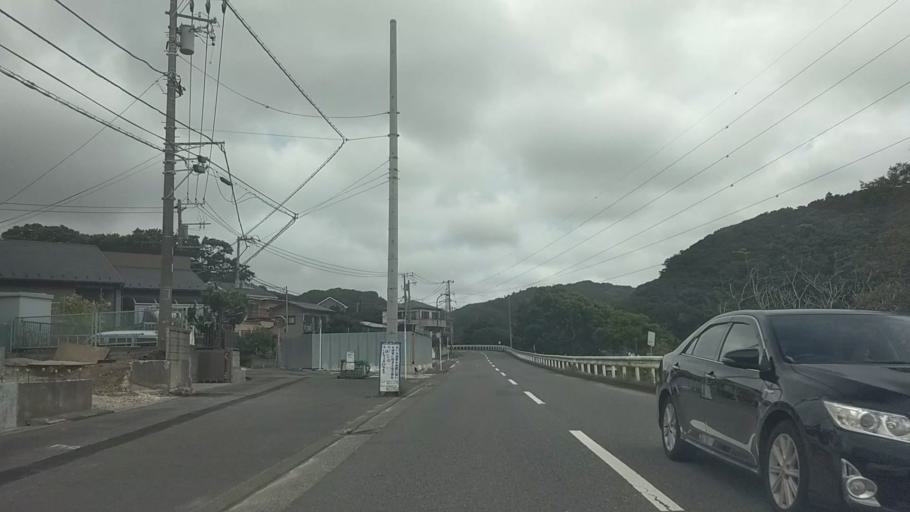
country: JP
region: Kanagawa
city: Yokosuka
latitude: 35.2307
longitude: 139.6320
